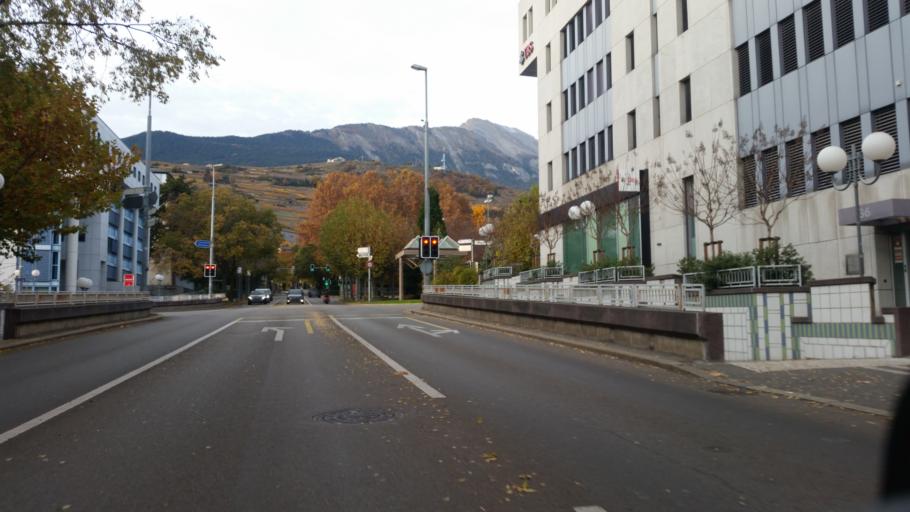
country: CH
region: Valais
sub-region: Sion District
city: Sitten
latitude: 46.2316
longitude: 7.3576
